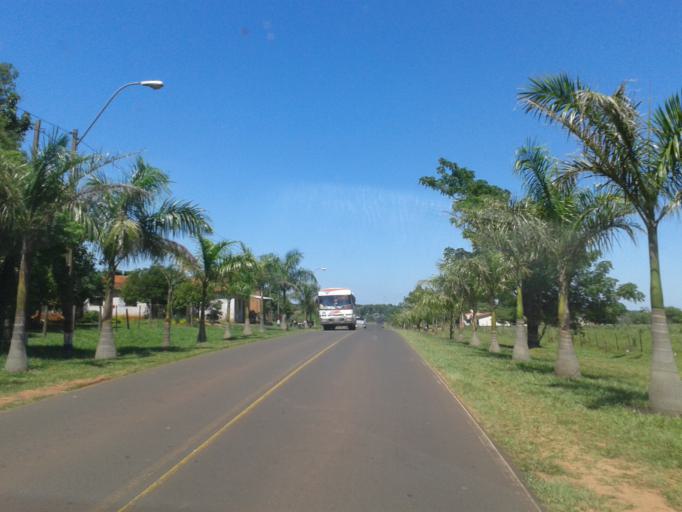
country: PY
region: Misiones
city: Santa Rosa
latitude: -26.8889
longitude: -56.8636
